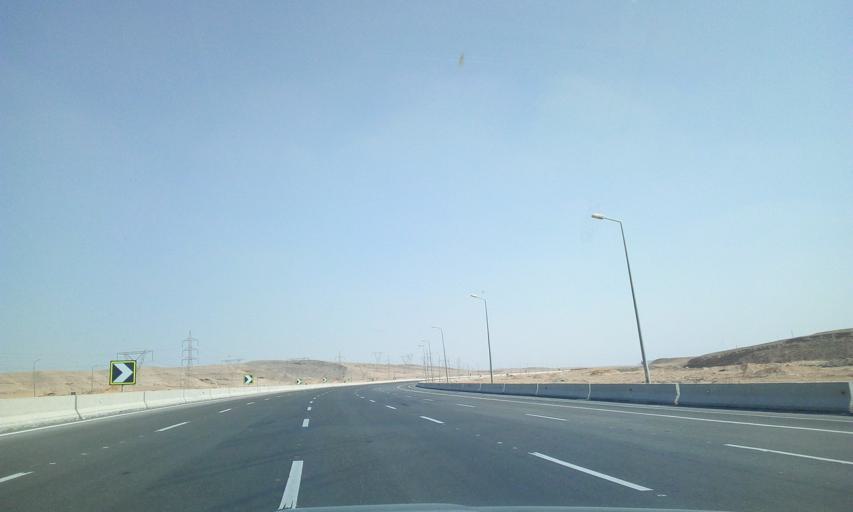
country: EG
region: As Suways
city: Ain Sukhna
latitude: 29.8222
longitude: 31.8902
